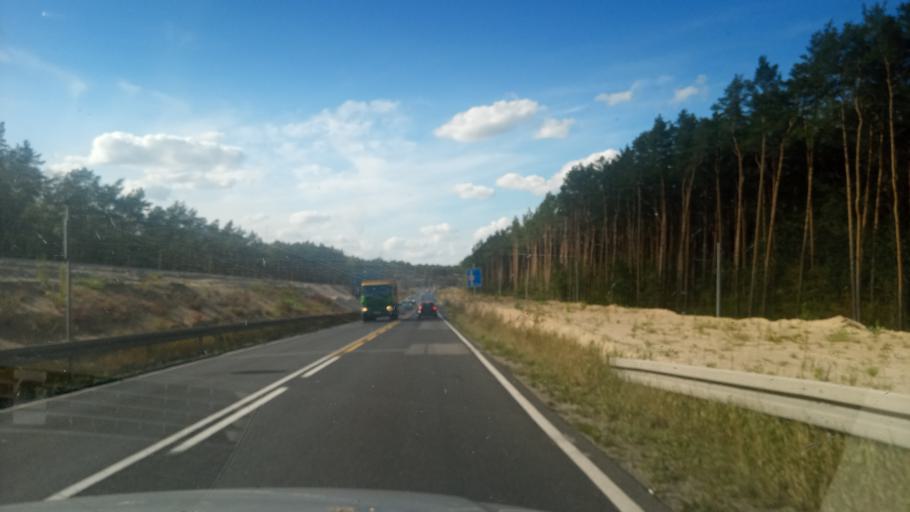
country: PL
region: Kujawsko-Pomorskie
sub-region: Powiat bydgoski
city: Biale Blota
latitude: 53.1018
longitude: 17.8903
